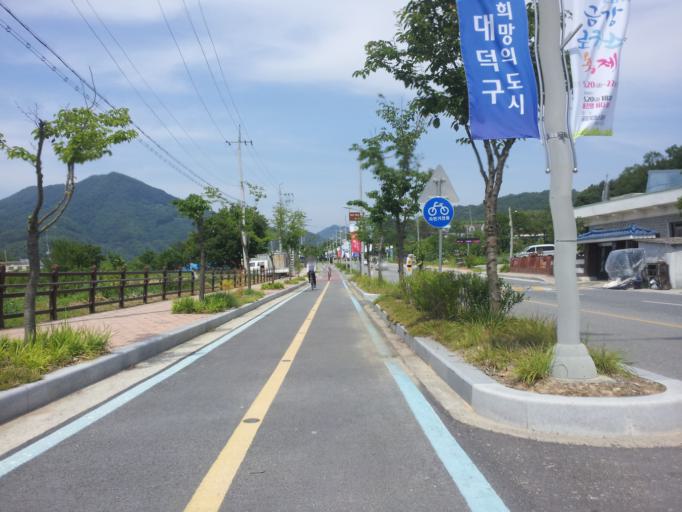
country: KR
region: Daejeon
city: Sintansin
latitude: 36.4658
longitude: 127.4678
